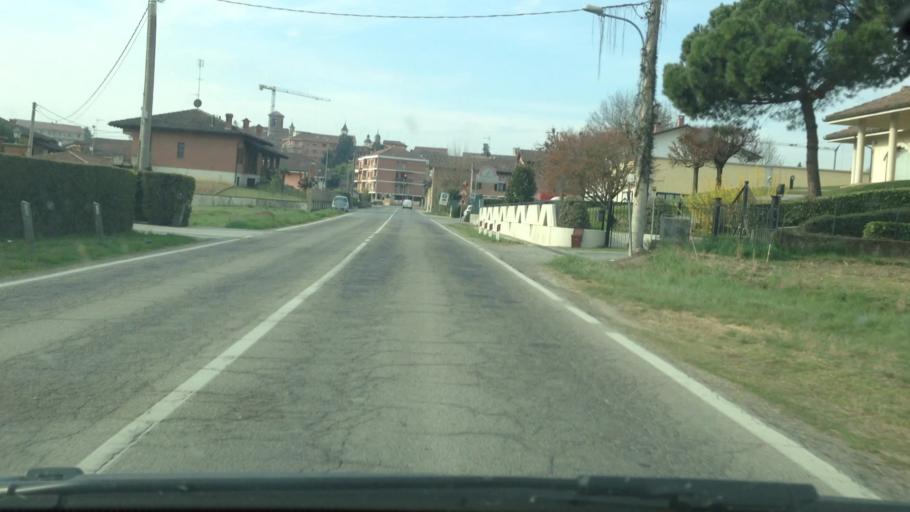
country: IT
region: Piedmont
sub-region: Provincia di Asti
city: San Damiano d'Asti
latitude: 44.8406
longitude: 8.0675
